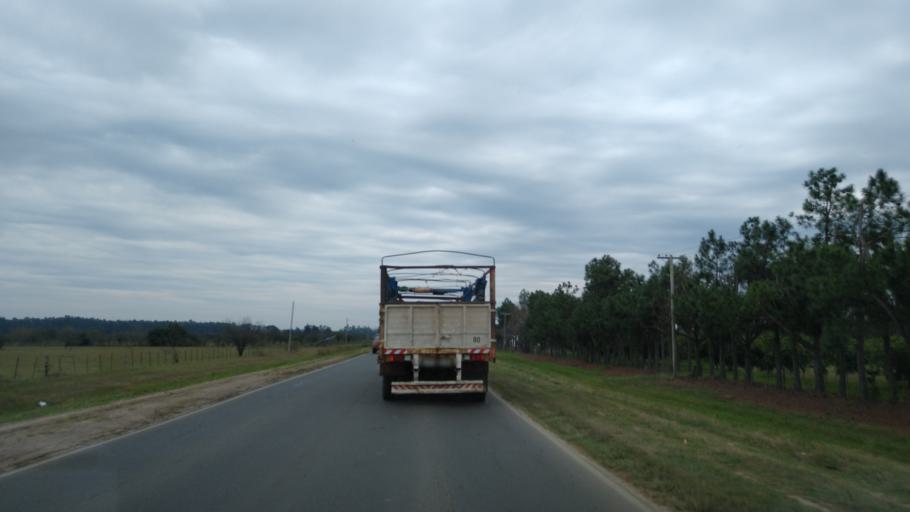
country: AR
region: Entre Rios
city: Villa del Rosario
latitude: -30.7905
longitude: -57.9433
